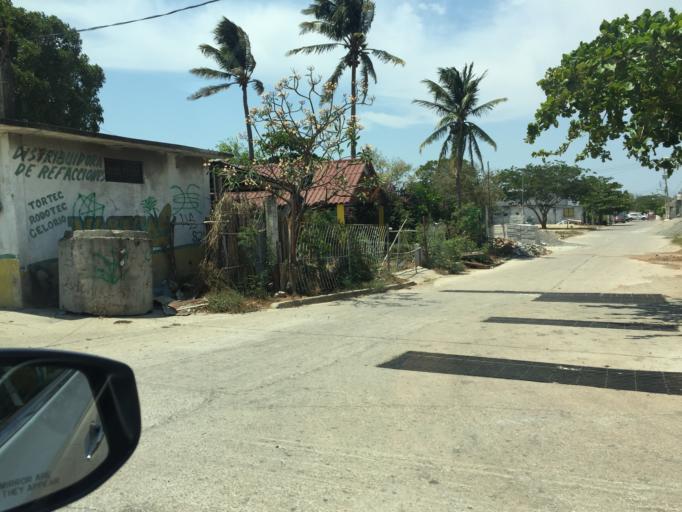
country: MX
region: Oaxaca
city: Asuncion Ixtaltepec
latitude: 16.5045
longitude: -95.0630
